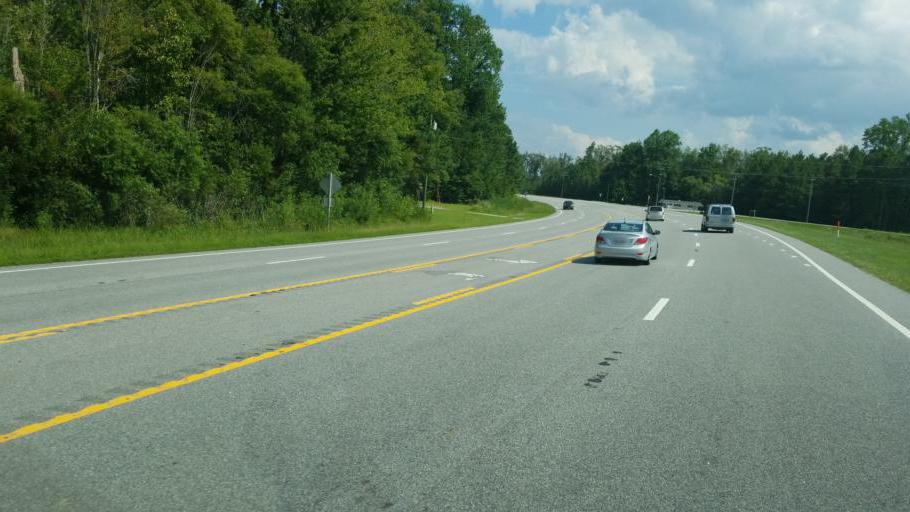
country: US
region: North Carolina
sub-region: Currituck County
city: Currituck
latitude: 36.4150
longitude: -76.0044
